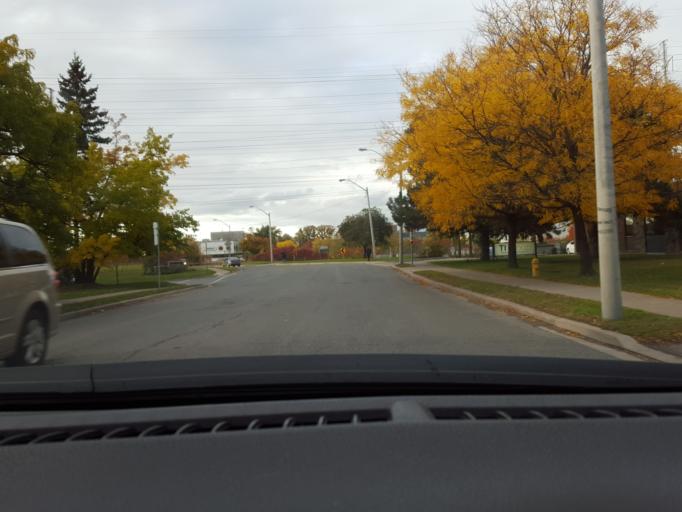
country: CA
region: Ontario
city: Toronto
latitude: 43.7088
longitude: -79.3442
